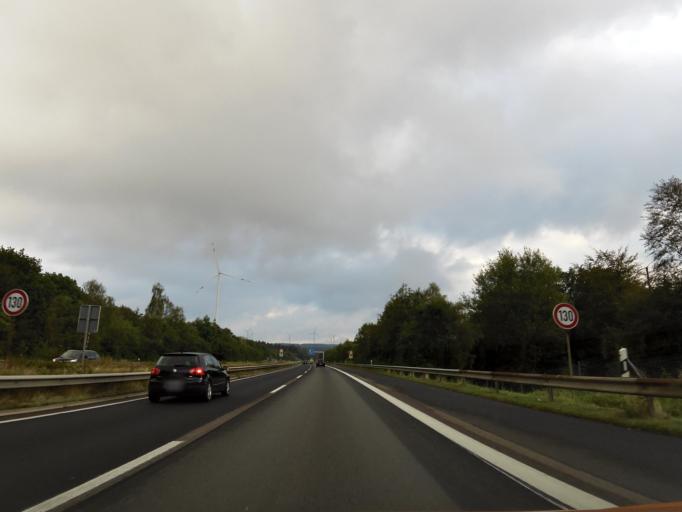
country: DE
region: Rheinland-Pfalz
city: Hungenroth
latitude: 50.1288
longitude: 7.5941
